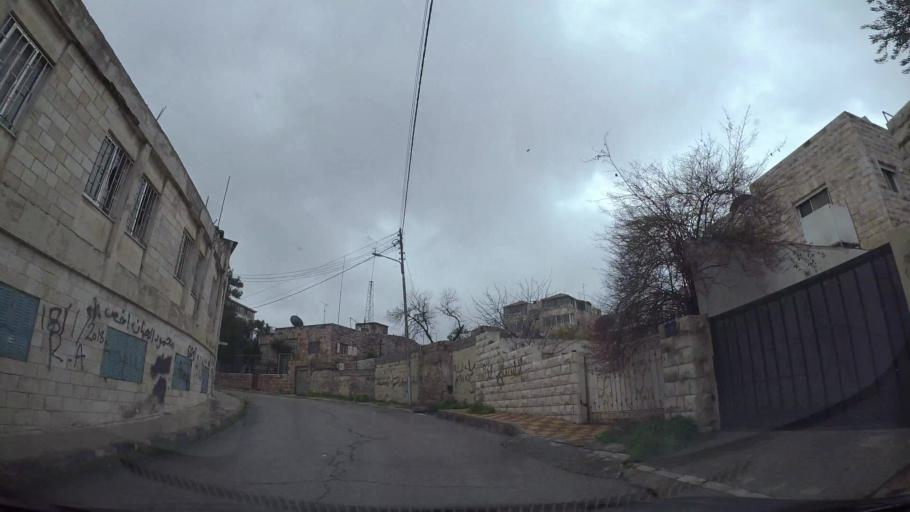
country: JO
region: Amman
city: Amman
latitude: 31.9496
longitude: 35.9218
